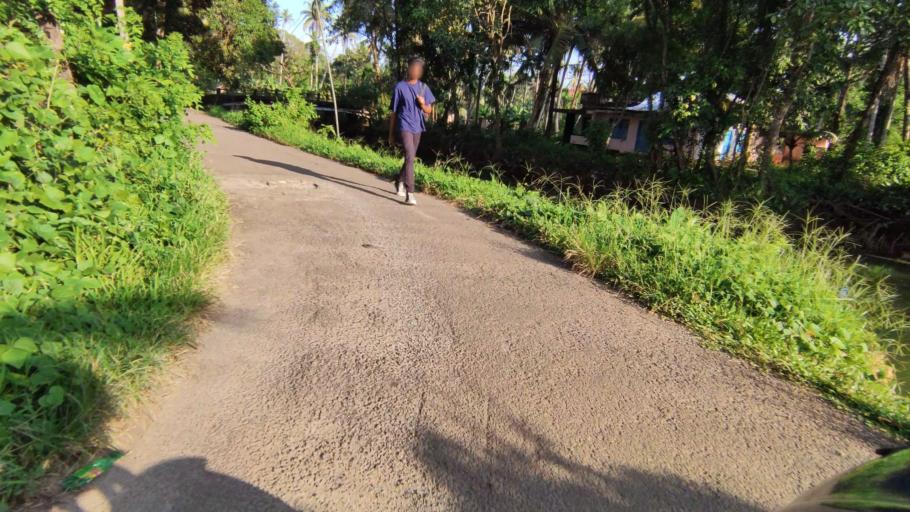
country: IN
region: Kerala
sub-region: Kottayam
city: Kottayam
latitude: 9.5940
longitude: 76.4837
